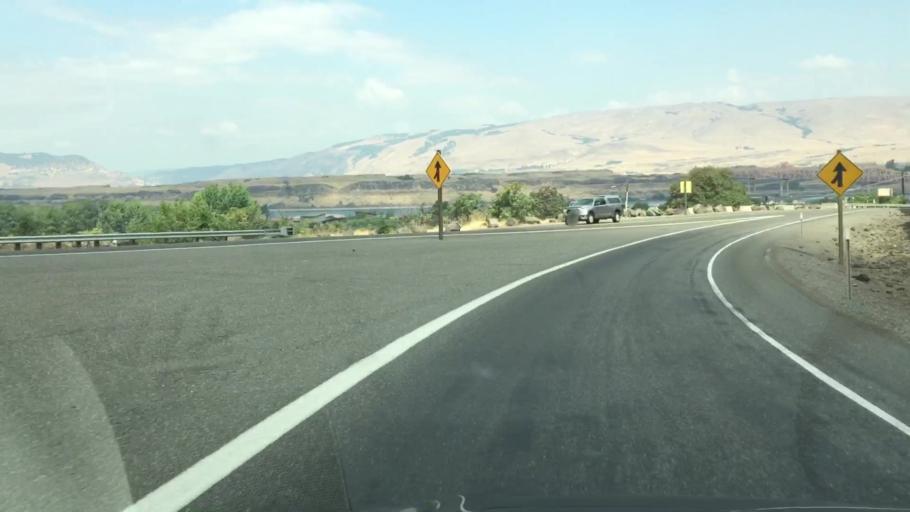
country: US
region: Oregon
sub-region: Wasco County
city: The Dalles
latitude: 45.5988
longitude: -121.1393
